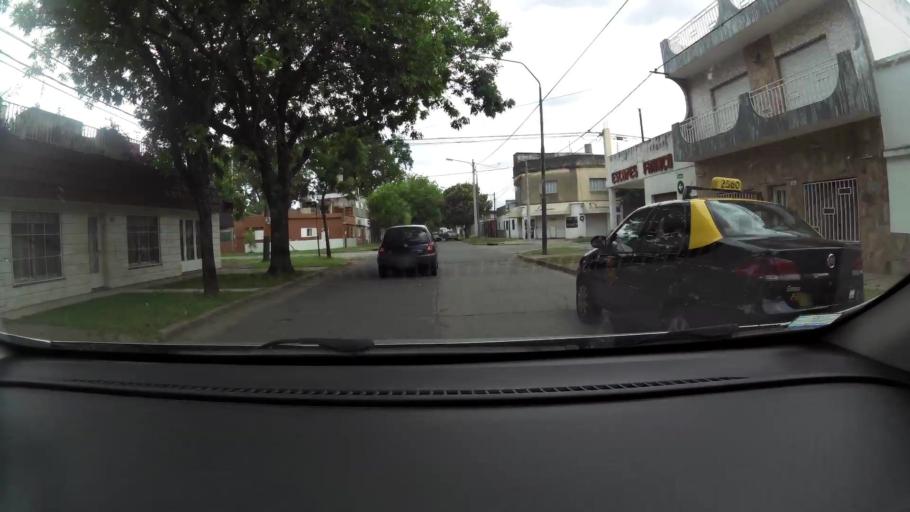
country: AR
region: Santa Fe
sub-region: Departamento de Rosario
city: Rosario
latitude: -32.9808
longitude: -60.6555
